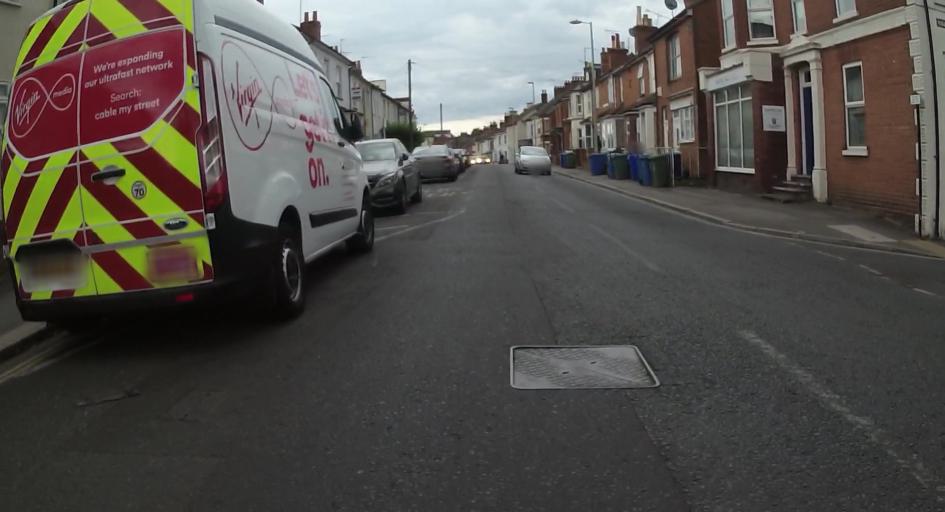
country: GB
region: England
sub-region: Hampshire
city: Aldershot
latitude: 51.2454
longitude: -0.7656
